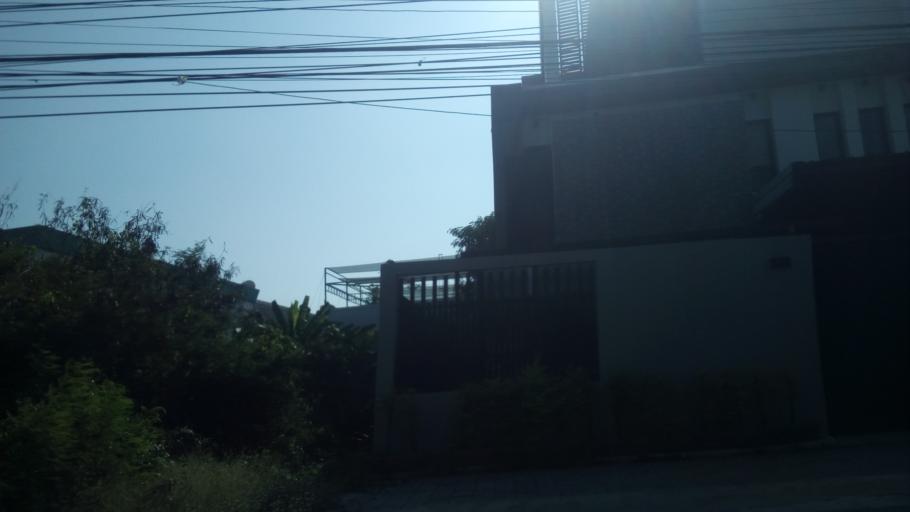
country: TH
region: Nakhon Pathom
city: Salaya
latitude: 13.8492
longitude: 100.3039
